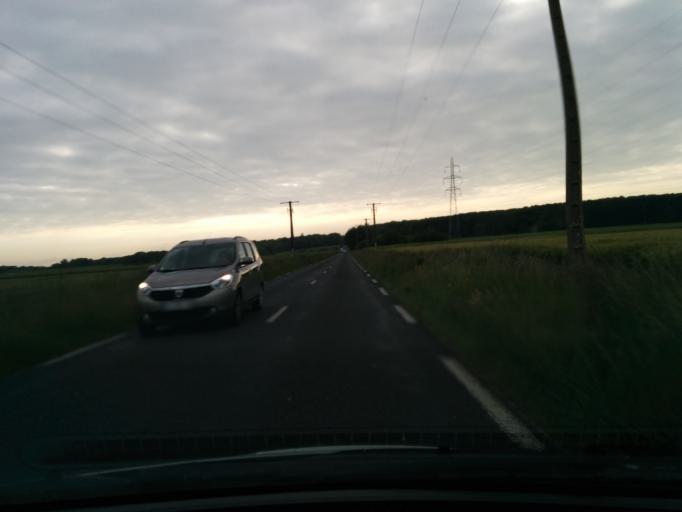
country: FR
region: Ile-de-France
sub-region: Departement des Yvelines
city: Limetz-Villez
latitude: 49.0945
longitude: 1.5626
